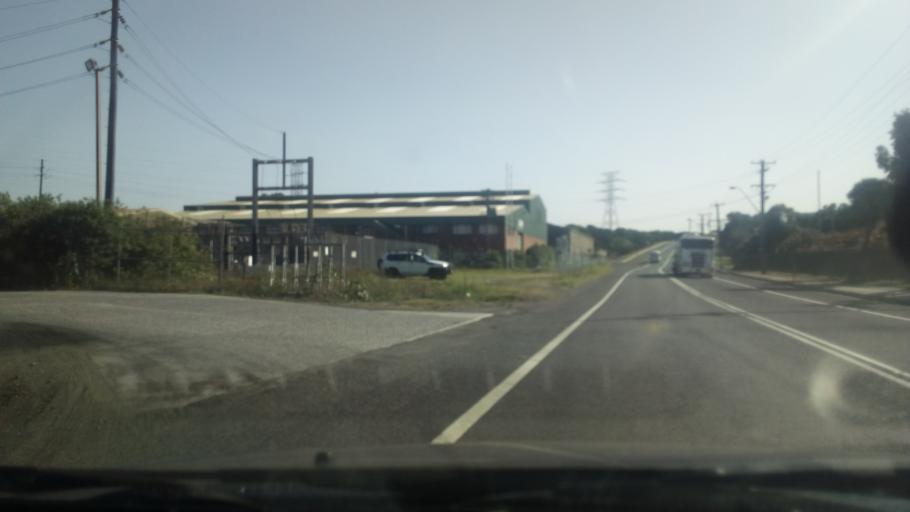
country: AU
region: New South Wales
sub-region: Wollongong
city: Cringila
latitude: -34.4711
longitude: 150.8921
